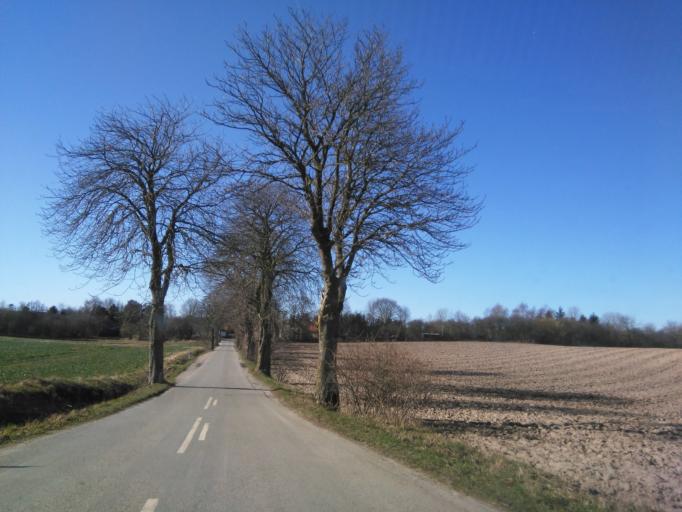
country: DK
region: Central Jutland
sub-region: Arhus Kommune
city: Marslet
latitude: 56.0639
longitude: 10.1781
